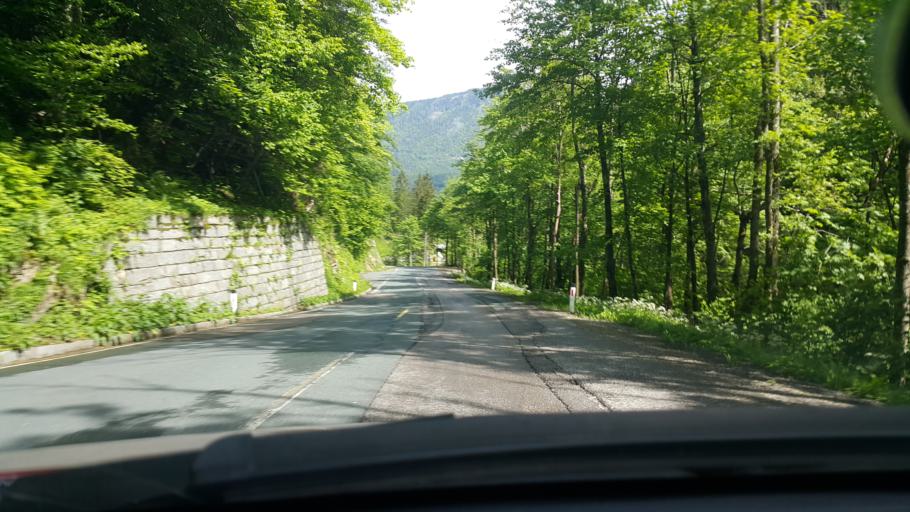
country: AT
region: Carinthia
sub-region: Politischer Bezirk Klagenfurt Land
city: Ferlach
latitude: 46.4623
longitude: 14.2578
